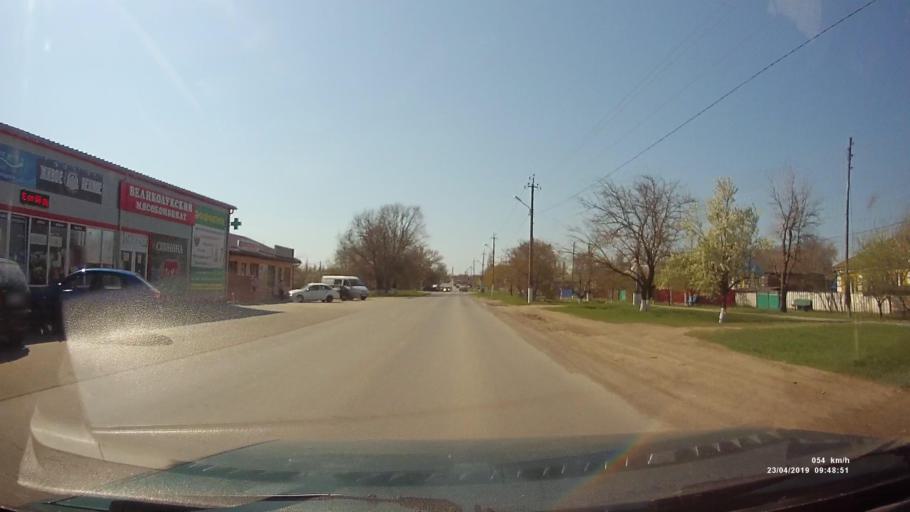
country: RU
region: Rostov
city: Orlovskiy
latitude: 46.8679
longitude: 42.0342
